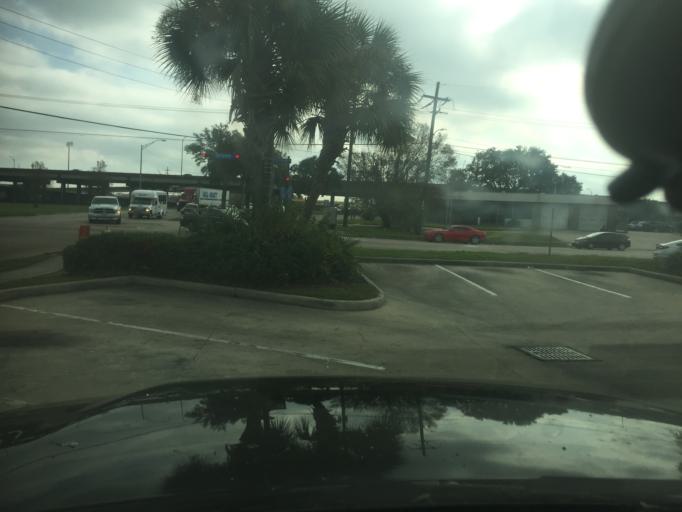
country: US
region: Louisiana
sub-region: Saint Bernard Parish
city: Arabi
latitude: 30.0043
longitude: -90.0360
